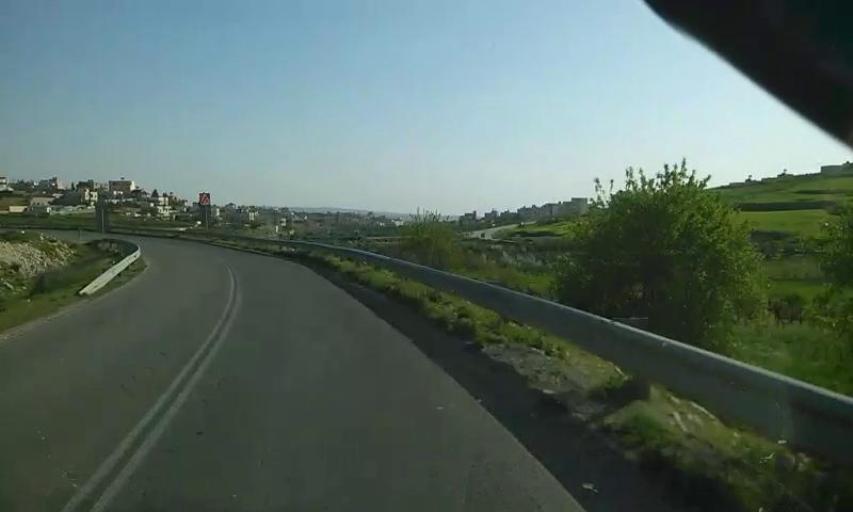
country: PS
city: Al Hilah
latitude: 31.4722
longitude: 35.1327
